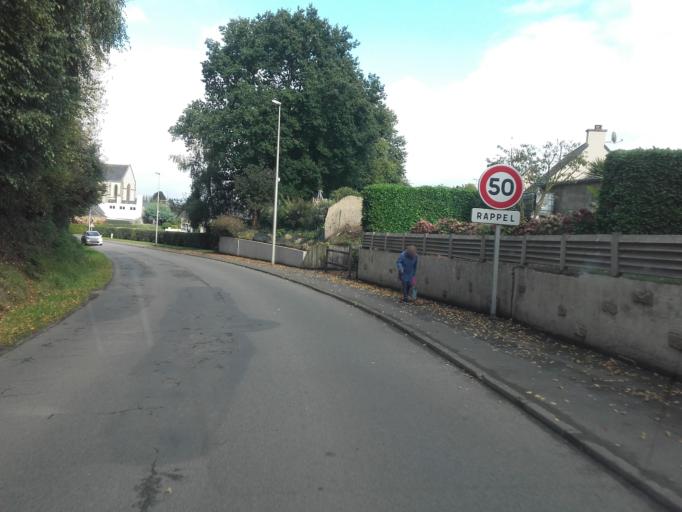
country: FR
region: Brittany
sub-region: Departement des Cotes-d'Armor
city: Plelo
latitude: 48.5545
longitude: -2.9489
